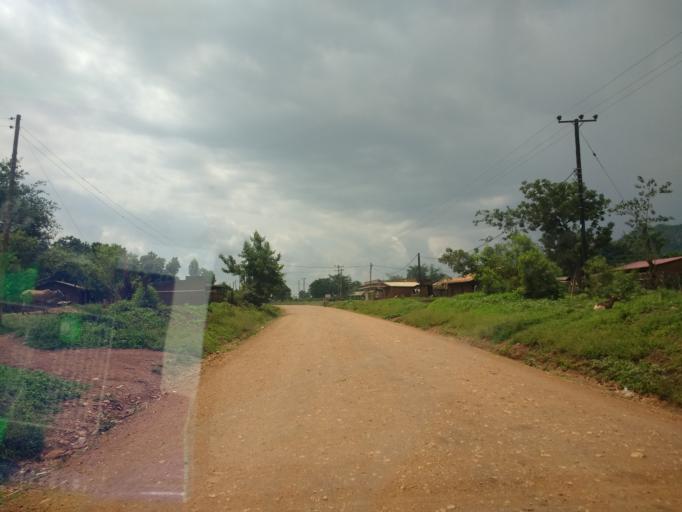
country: UG
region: Eastern Region
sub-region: Sironko District
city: Sironko
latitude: 1.3382
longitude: 34.2989
